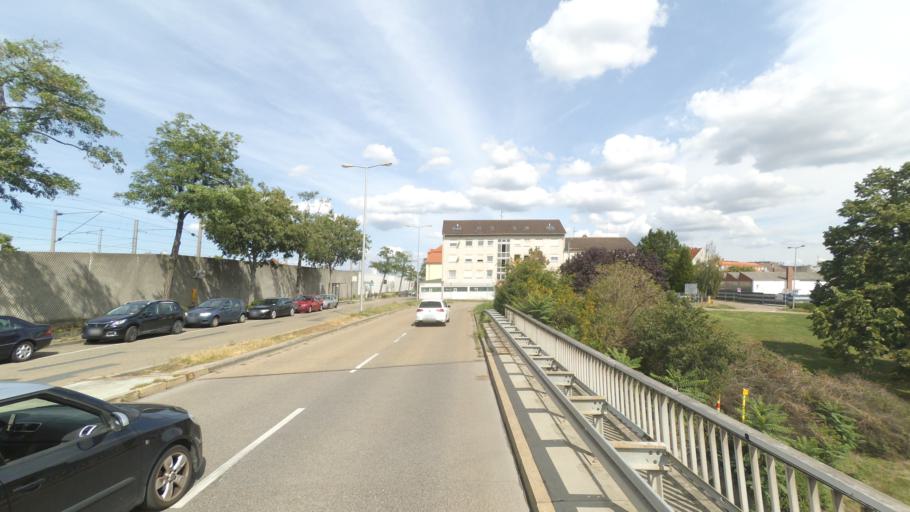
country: DE
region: Baden-Wuerttemberg
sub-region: Karlsruhe Region
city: Mannheim
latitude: 49.5153
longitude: 8.4757
